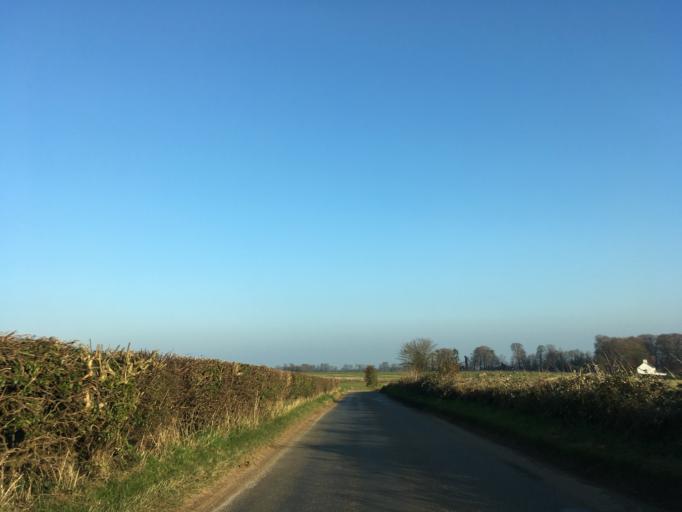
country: GB
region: England
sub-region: South Gloucestershire
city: Horton
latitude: 51.5557
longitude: -2.3296
